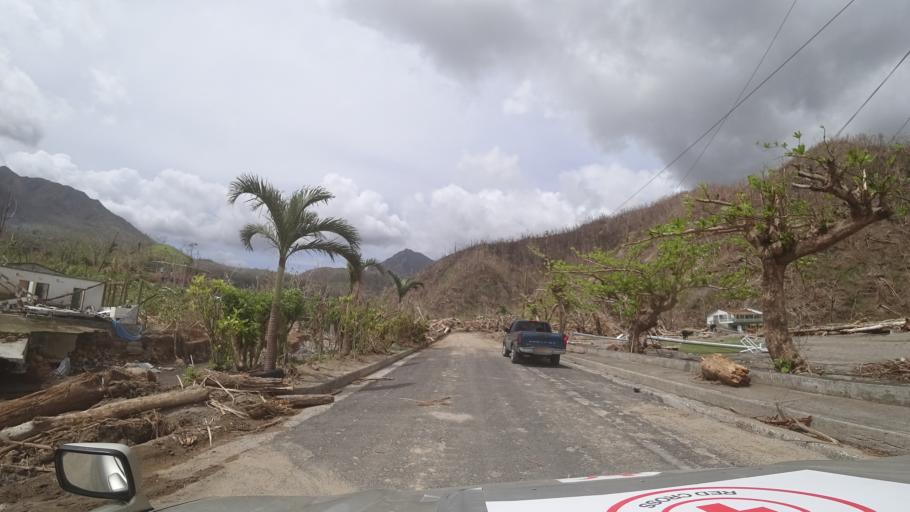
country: DM
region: Saint Patrick
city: Berekua
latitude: 15.2463
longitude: -61.3113
